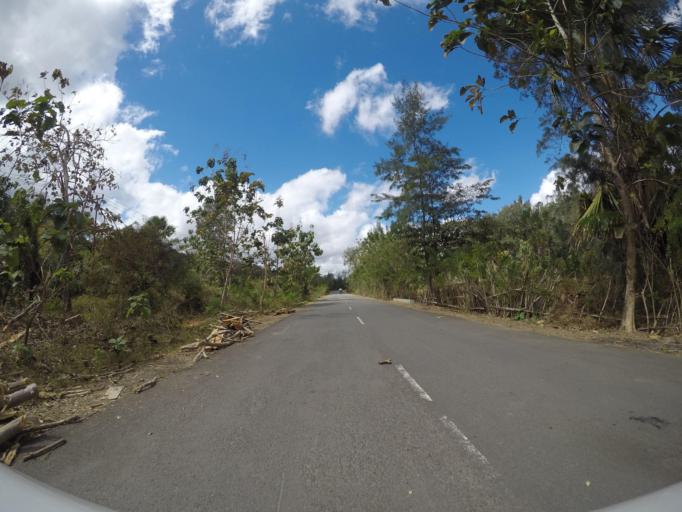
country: TL
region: Lautem
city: Lospalos
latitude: -8.4647
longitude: 126.8208
